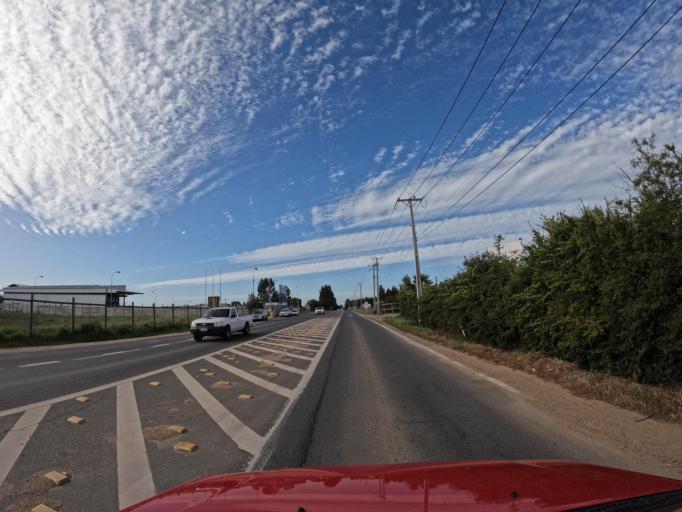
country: CL
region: Valparaiso
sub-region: San Antonio Province
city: San Antonio
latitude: -34.1440
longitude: -71.7310
